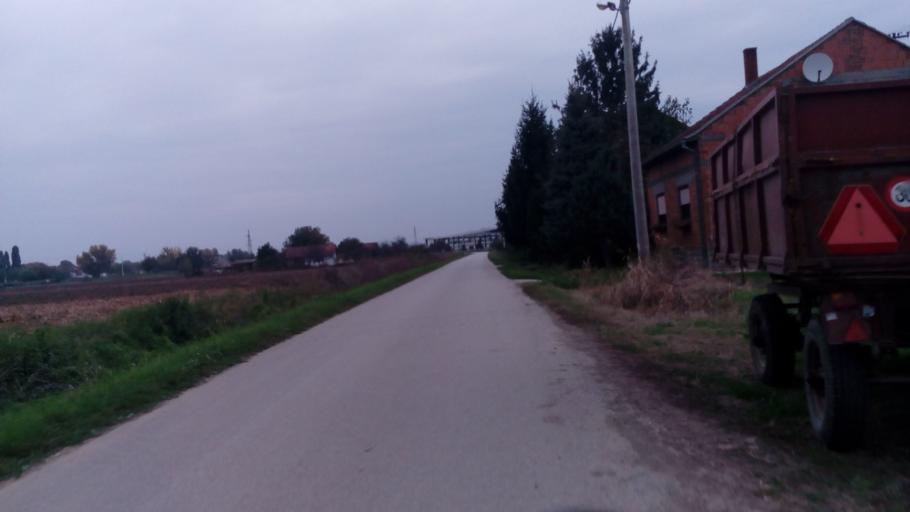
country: HR
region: Vukovarsko-Srijemska
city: Vinkovci
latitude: 45.2703
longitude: 18.8132
